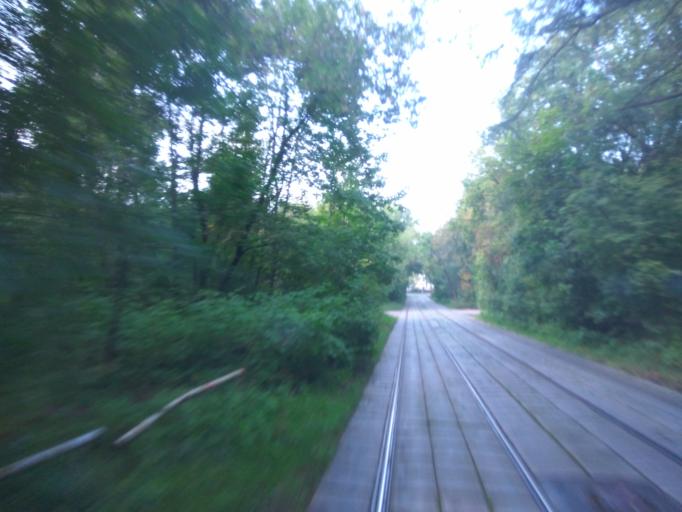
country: RU
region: Moscow
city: Sokol'niki
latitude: 55.8042
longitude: 37.6902
